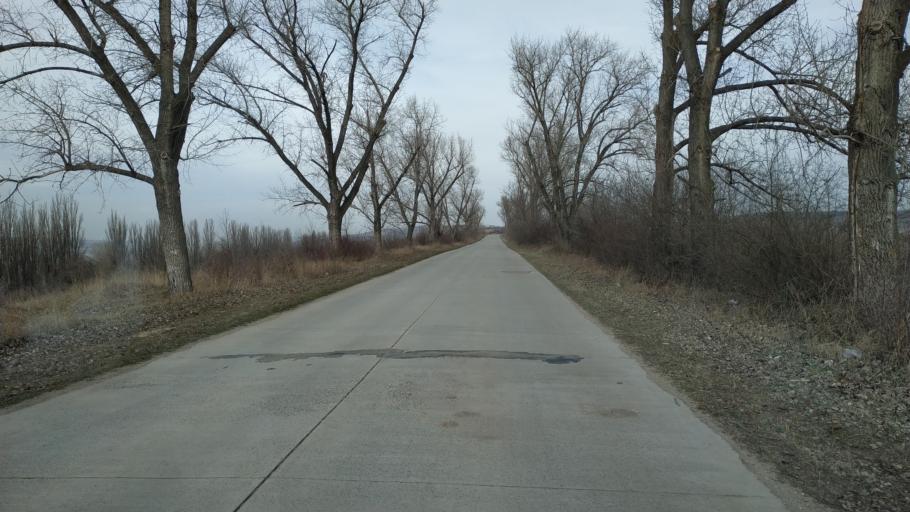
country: MD
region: Chisinau
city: Vatra
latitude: 47.0968
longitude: 28.7343
